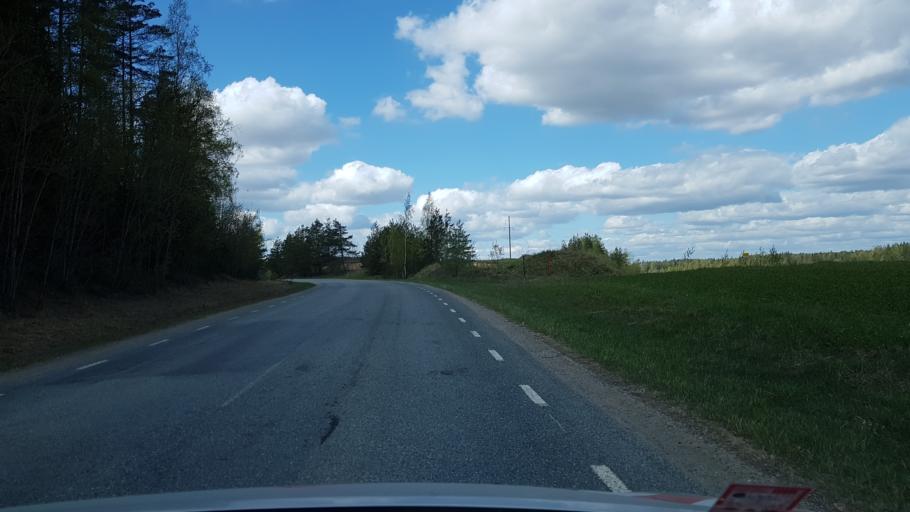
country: EE
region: Jogevamaa
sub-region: Jogeva linn
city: Jogeva
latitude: 58.7326
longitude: 26.3221
